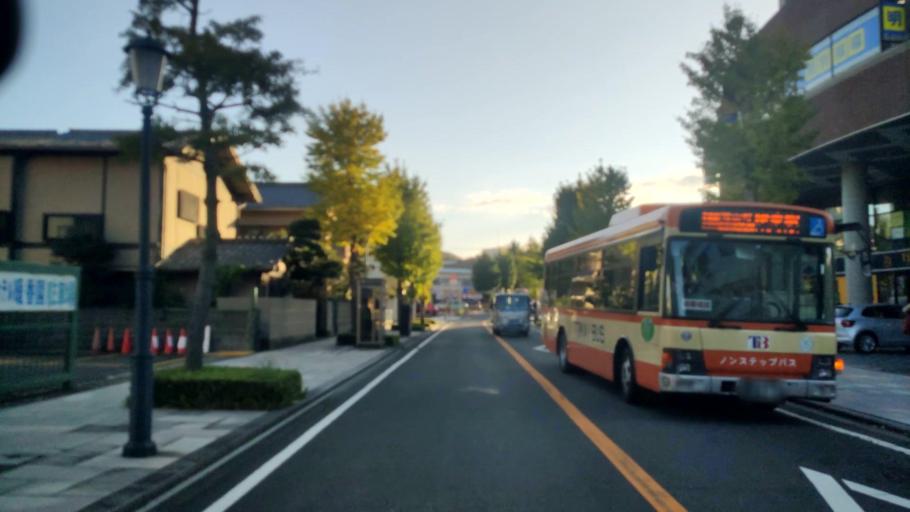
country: JP
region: Shizuoka
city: Ito
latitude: 34.9686
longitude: 139.0971
